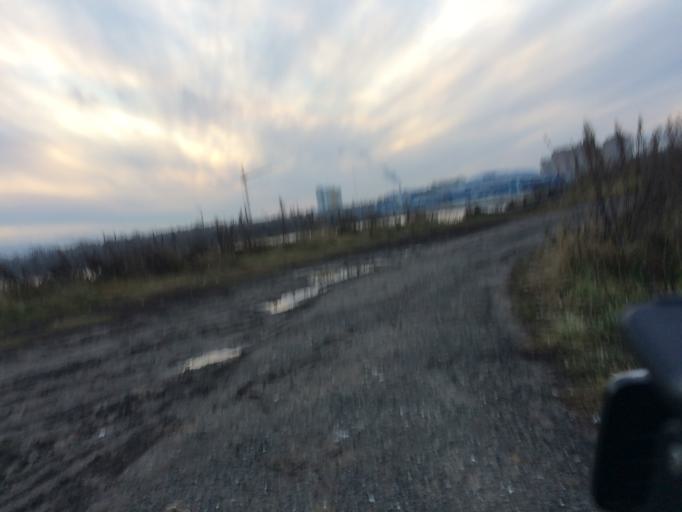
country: RU
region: Mariy-El
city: Yoshkar-Ola
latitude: 56.6255
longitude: 47.9045
